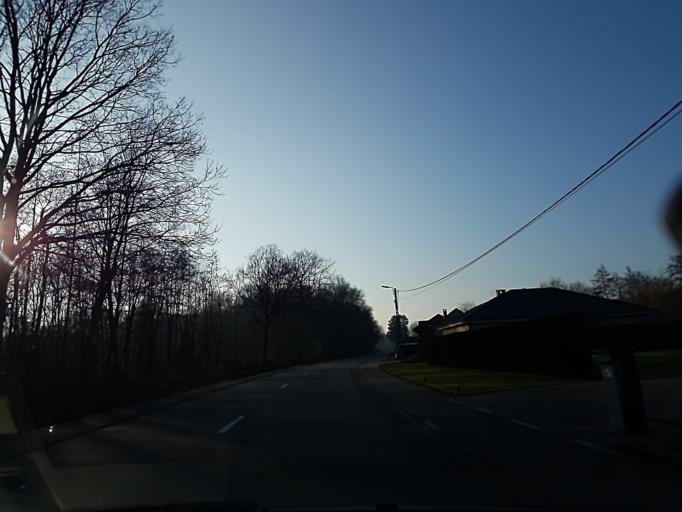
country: BE
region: Flanders
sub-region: Provincie Vlaams-Brabant
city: Tremelo
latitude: 51.0181
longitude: 4.7392
